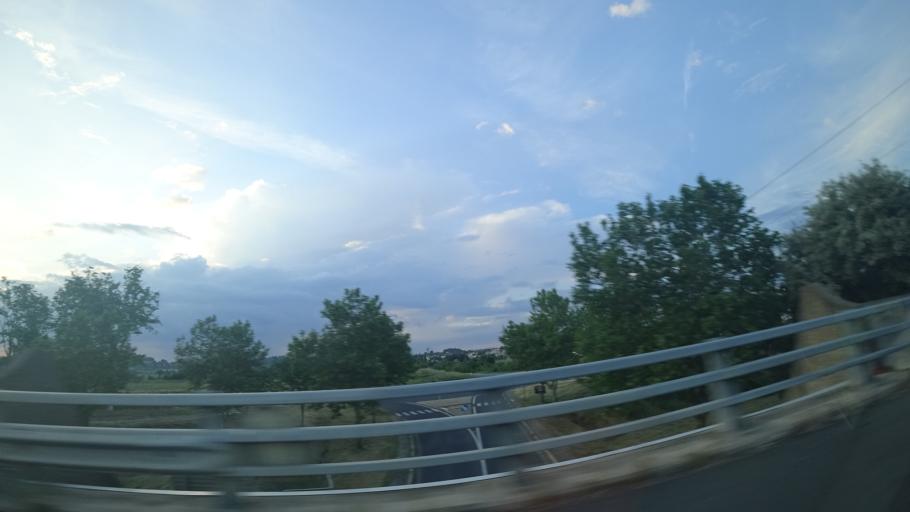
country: FR
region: Languedoc-Roussillon
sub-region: Departement de l'Herault
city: Pezenas
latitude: 43.4458
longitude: 3.4077
